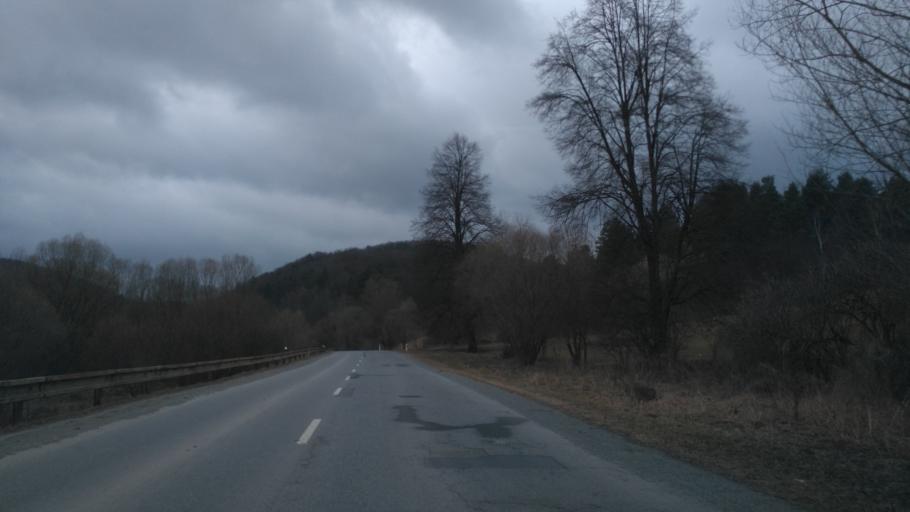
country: SK
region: Presovsky
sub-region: Okres Presov
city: Presov
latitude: 48.9597
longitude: 21.1125
